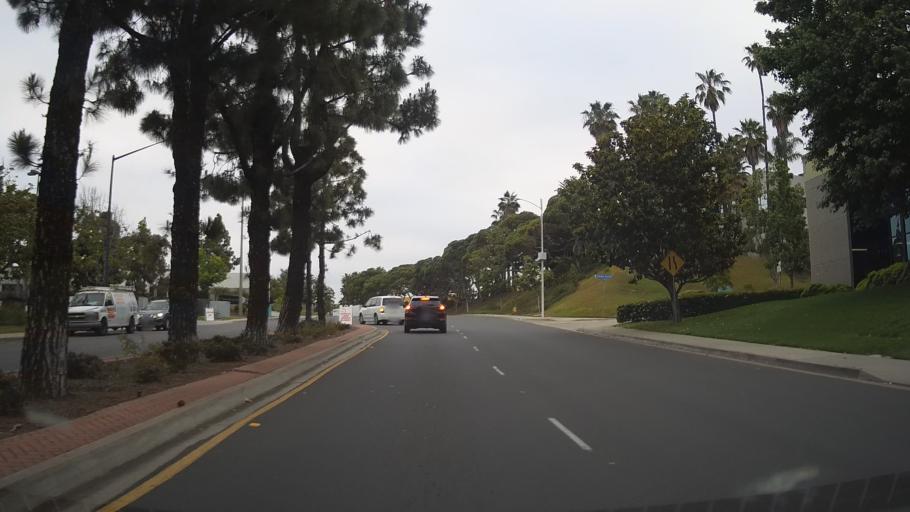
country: US
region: California
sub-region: San Diego County
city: National City
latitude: 32.7126
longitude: -117.1135
